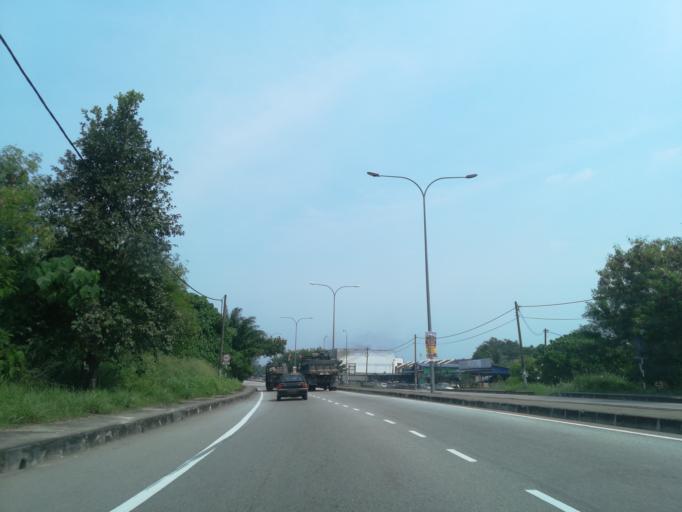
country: MY
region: Kedah
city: Kulim
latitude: 5.4073
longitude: 100.5513
